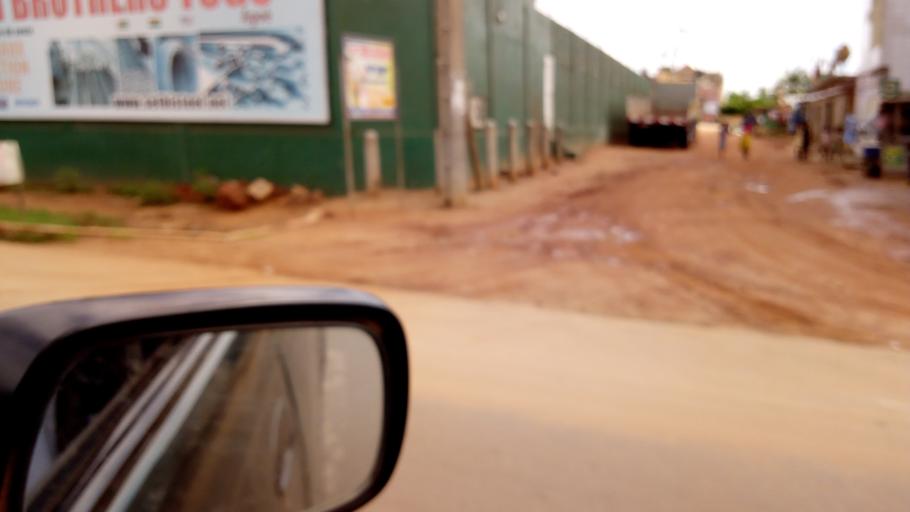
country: TG
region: Maritime
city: Lome
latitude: 6.2374
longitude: 1.2105
